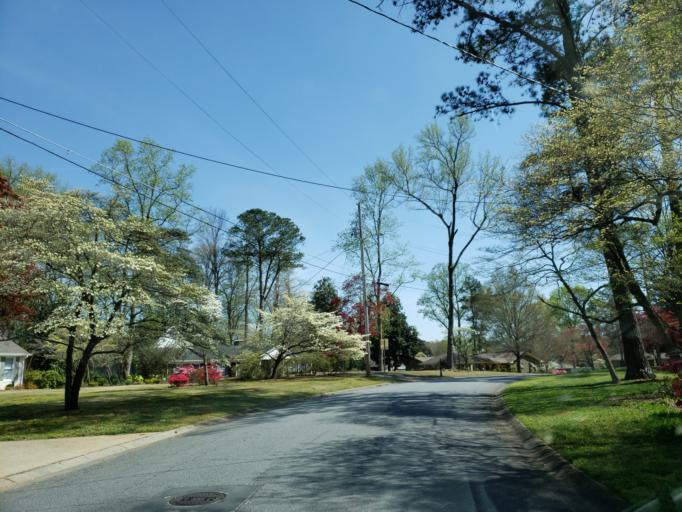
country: US
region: Georgia
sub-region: Cobb County
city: Marietta
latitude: 33.9621
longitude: -84.5607
